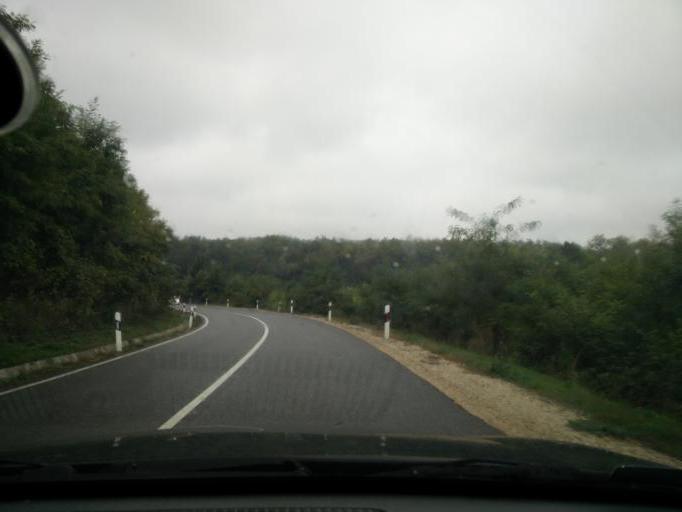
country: HU
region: Komarom-Esztergom
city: Bajna
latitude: 47.6363
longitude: 18.5607
